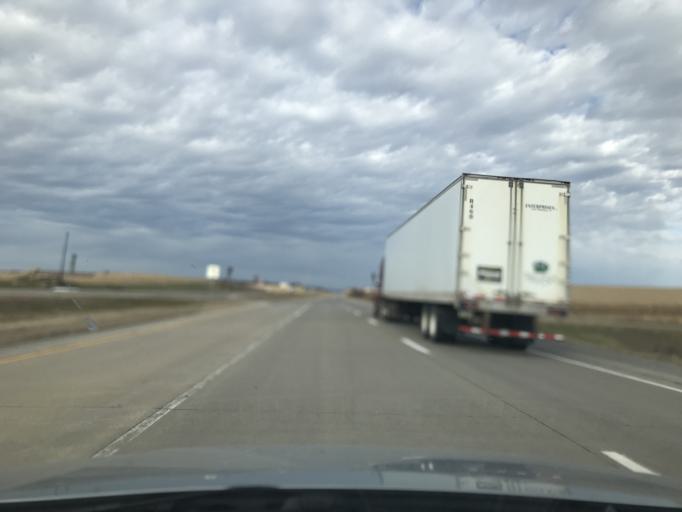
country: US
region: Illinois
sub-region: Jo Daviess County
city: East Dubuque
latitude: 42.3887
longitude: -90.6942
